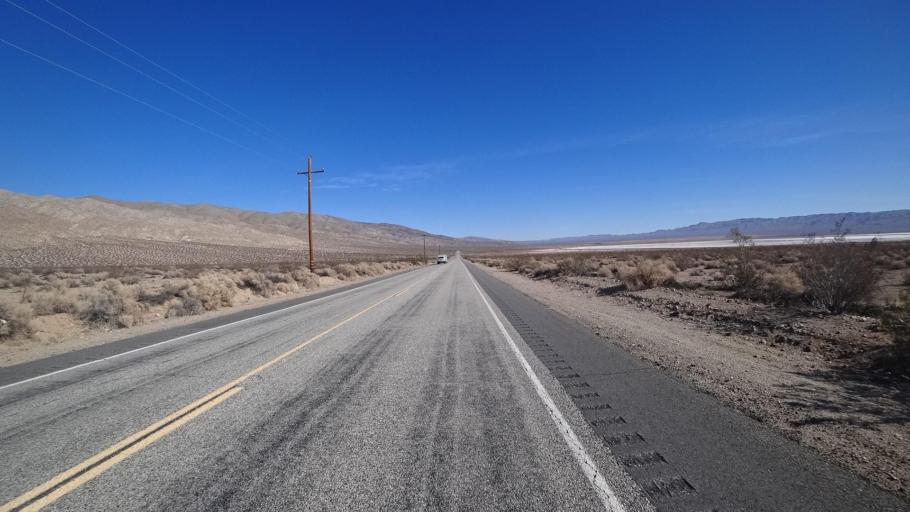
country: US
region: California
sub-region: Kern County
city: California City
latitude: 35.3645
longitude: -117.8929
